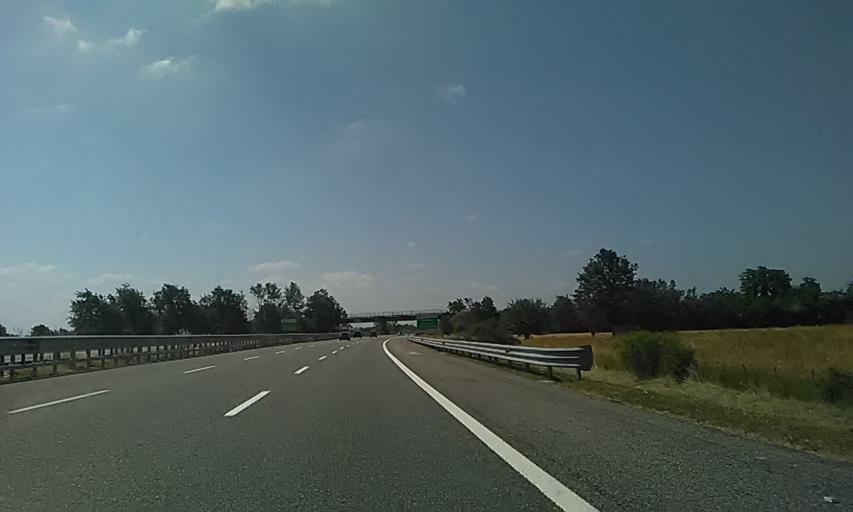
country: IT
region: Piedmont
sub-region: Provincia di Alessandria
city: Castellazzo Bormida
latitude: 44.8432
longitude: 8.5961
